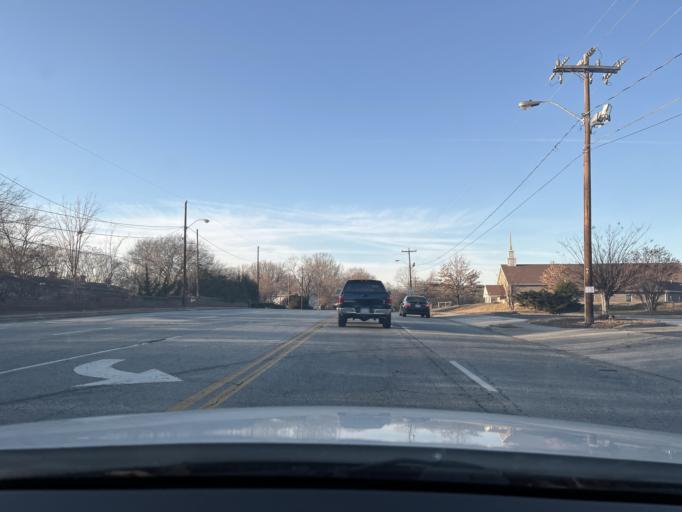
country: US
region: North Carolina
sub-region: Guilford County
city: Greensboro
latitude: 36.0538
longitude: -79.7925
